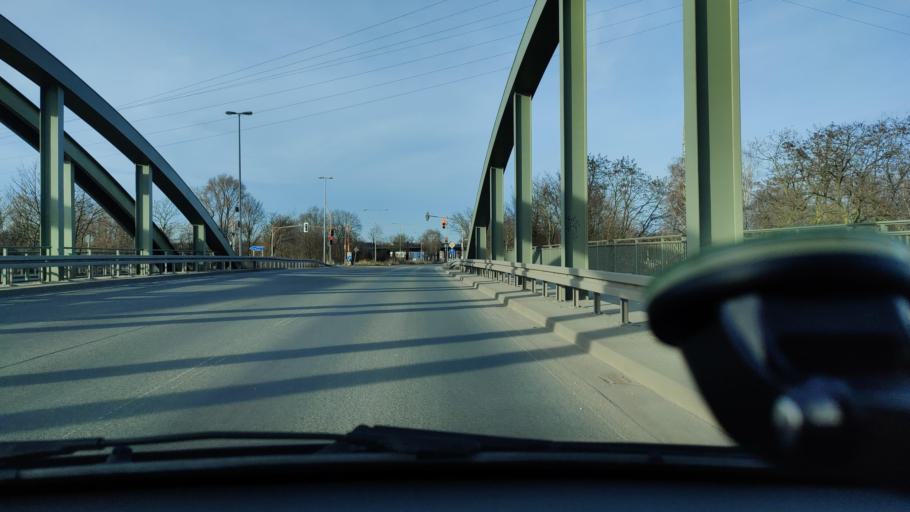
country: DE
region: North Rhine-Westphalia
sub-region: Regierungsbezirk Dusseldorf
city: Oberhausen
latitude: 51.4882
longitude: 6.8392
